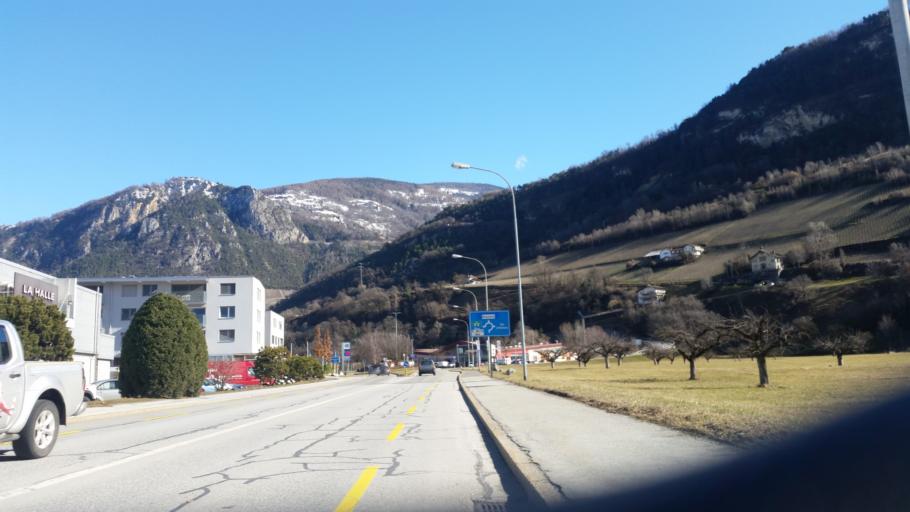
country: CH
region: Valais
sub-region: Herens District
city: Vex
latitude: 46.2269
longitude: 7.3841
